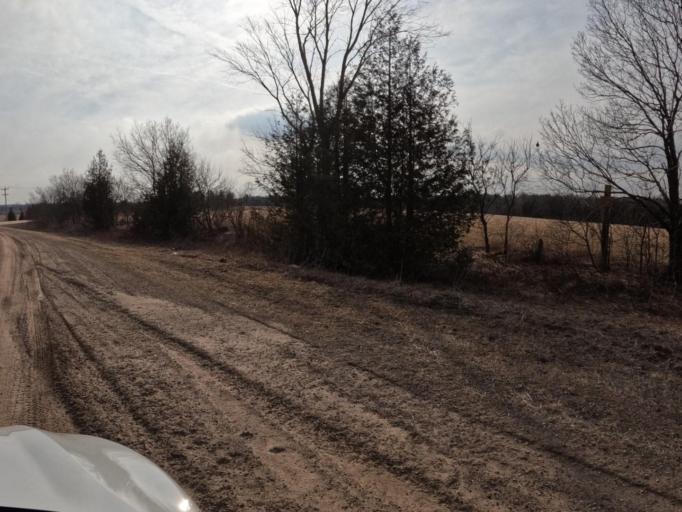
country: CA
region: Ontario
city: Orangeville
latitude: 43.9135
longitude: -80.2625
